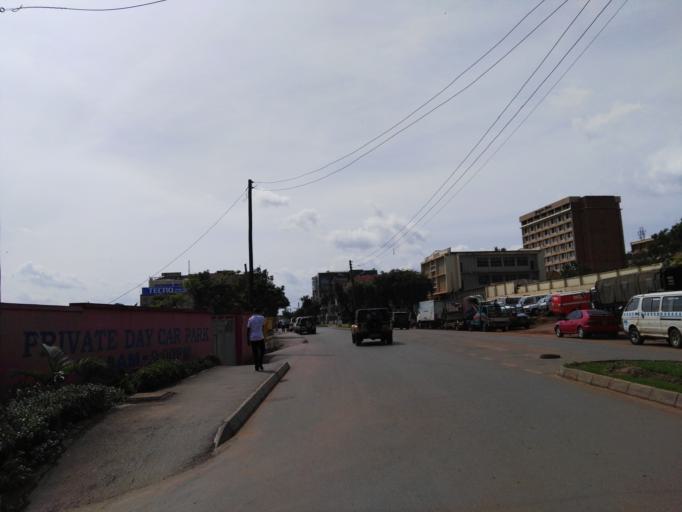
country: UG
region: Central Region
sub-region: Kampala District
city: Kampala
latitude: 0.3157
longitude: 32.5781
